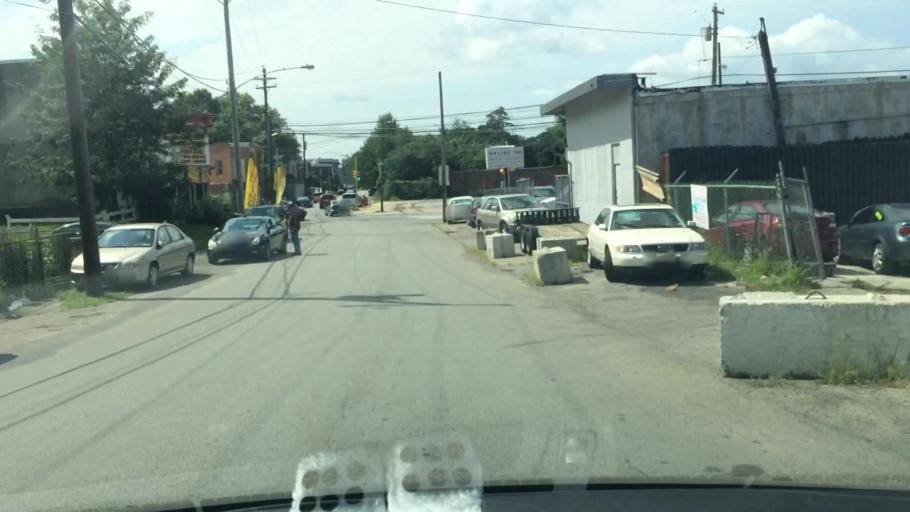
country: US
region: Pennsylvania
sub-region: Delaware County
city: Yeadon
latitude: 39.9288
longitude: -75.2346
